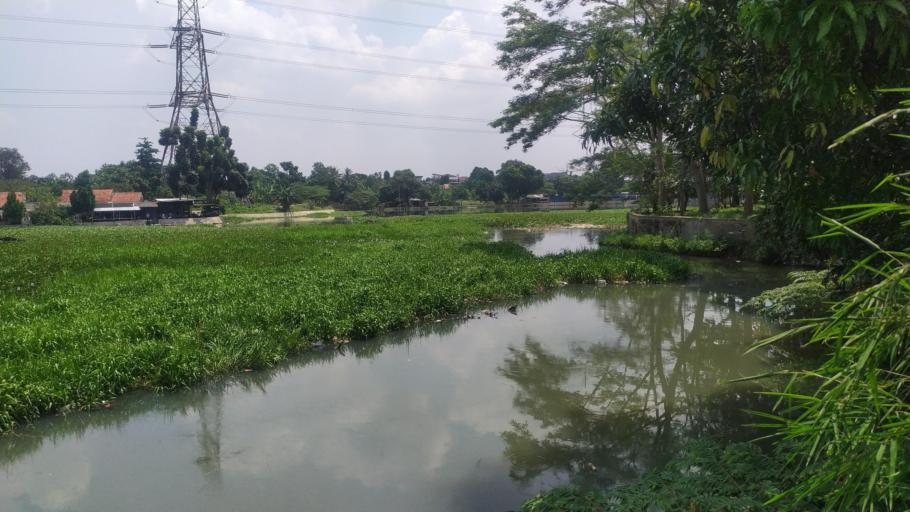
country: ID
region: West Java
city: Pamulang
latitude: -6.3453
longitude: 106.7256
